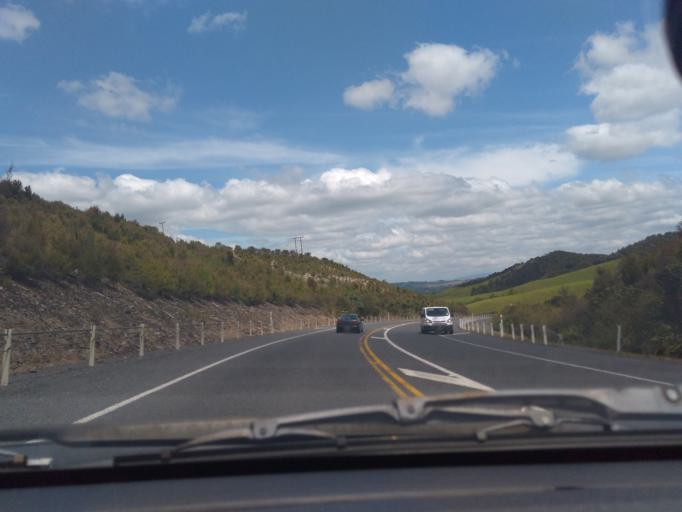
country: NZ
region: Northland
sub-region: Far North District
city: Kerikeri
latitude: -35.2726
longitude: 173.9481
